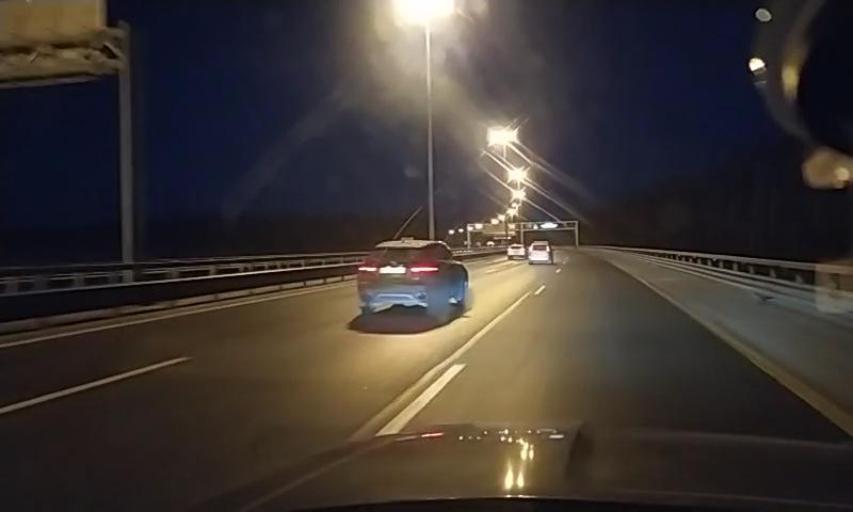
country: RU
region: St.-Petersburg
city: Pesochnyy
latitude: 60.0697
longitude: 30.1371
